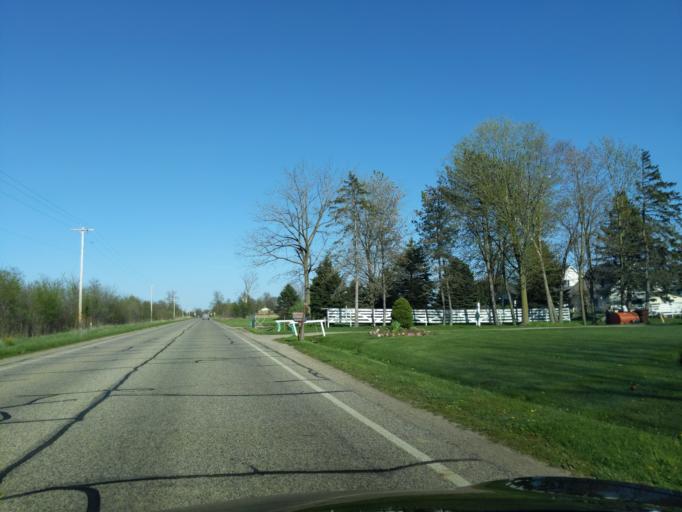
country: US
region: Michigan
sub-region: Ionia County
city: Portland
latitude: 42.8858
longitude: -85.0020
